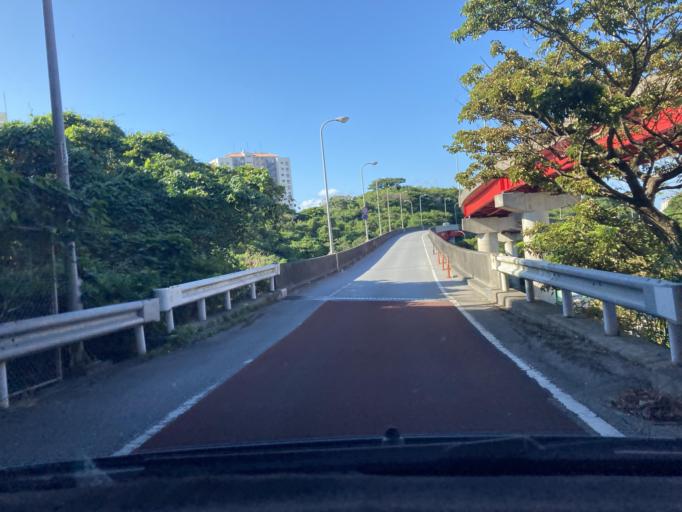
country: JP
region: Okinawa
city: Ginowan
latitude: 26.2556
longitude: 127.7288
